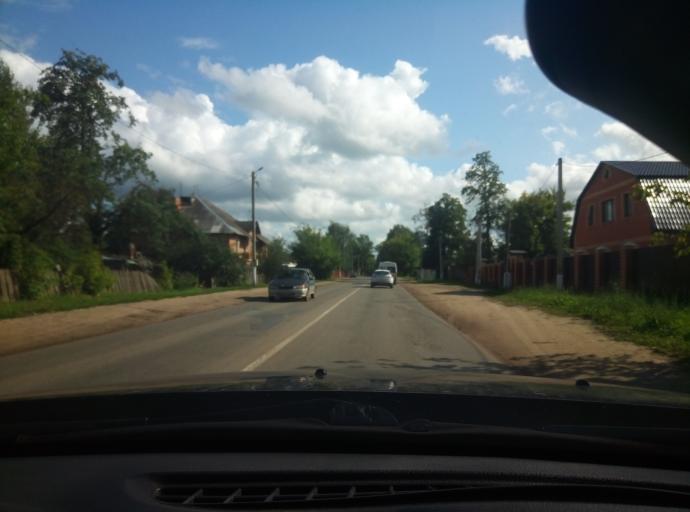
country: RU
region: Tula
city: Donskoy
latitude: 53.9795
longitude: 38.3098
